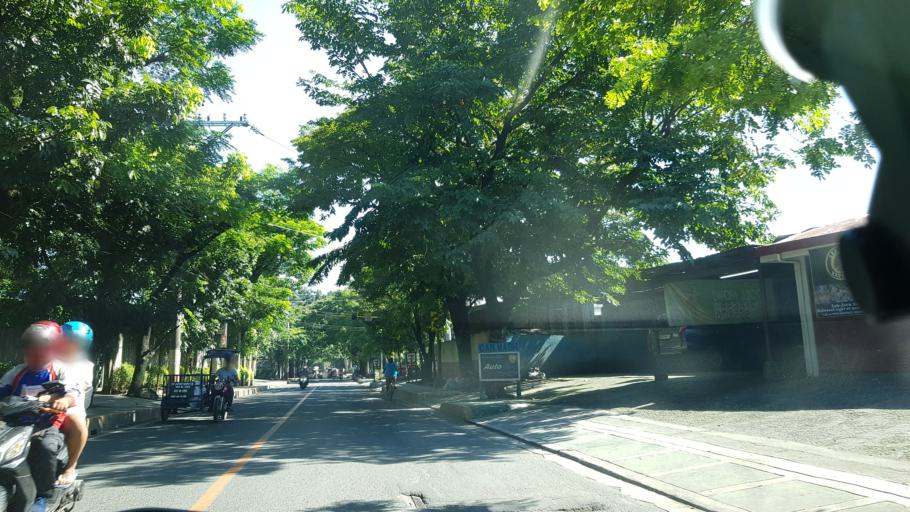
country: PH
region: Metro Manila
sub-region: Pasig
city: Pasig City
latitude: 14.5719
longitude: 121.0878
